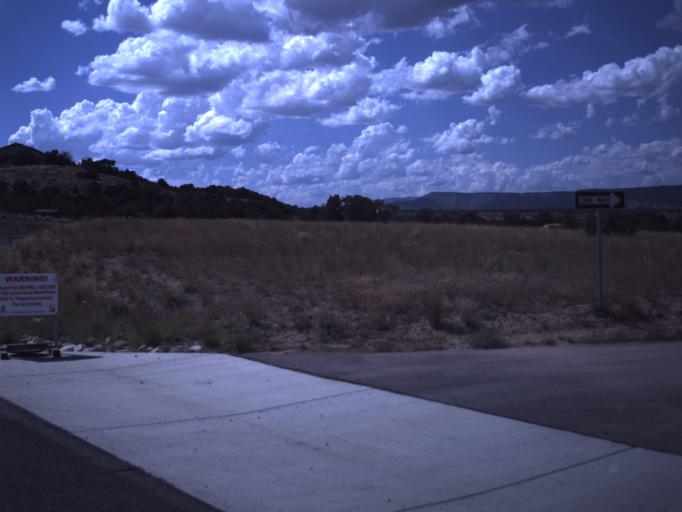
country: US
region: Utah
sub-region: Duchesne County
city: Duchesne
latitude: 40.1887
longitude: -110.4524
